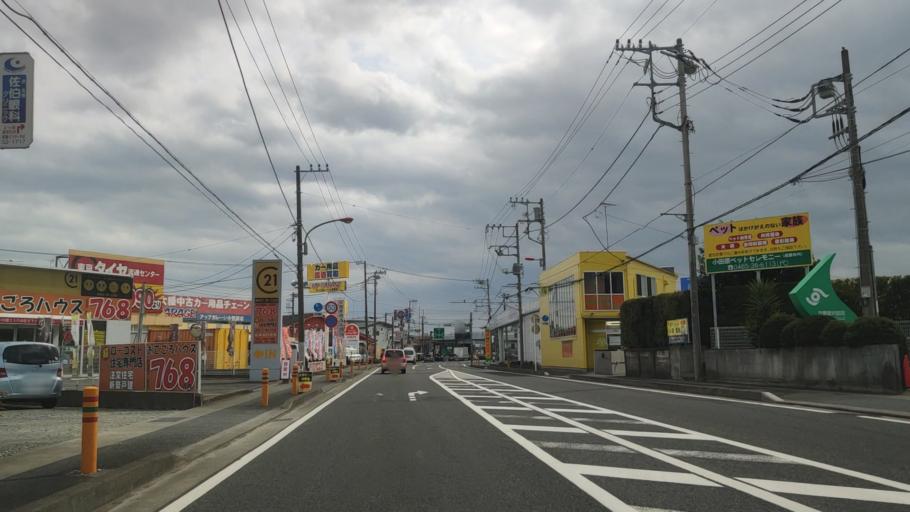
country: JP
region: Kanagawa
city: Odawara
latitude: 35.2882
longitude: 139.1686
